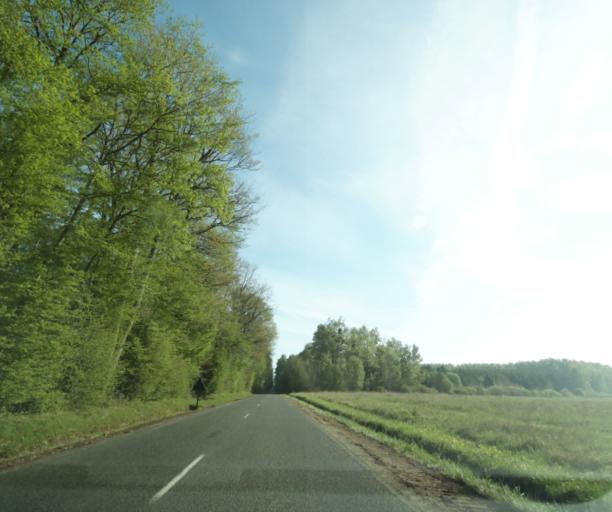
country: FR
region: Ile-de-France
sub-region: Departement de Seine-et-Marne
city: Vernou-la-Celle-sur-Seine
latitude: 48.4094
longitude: 2.8381
